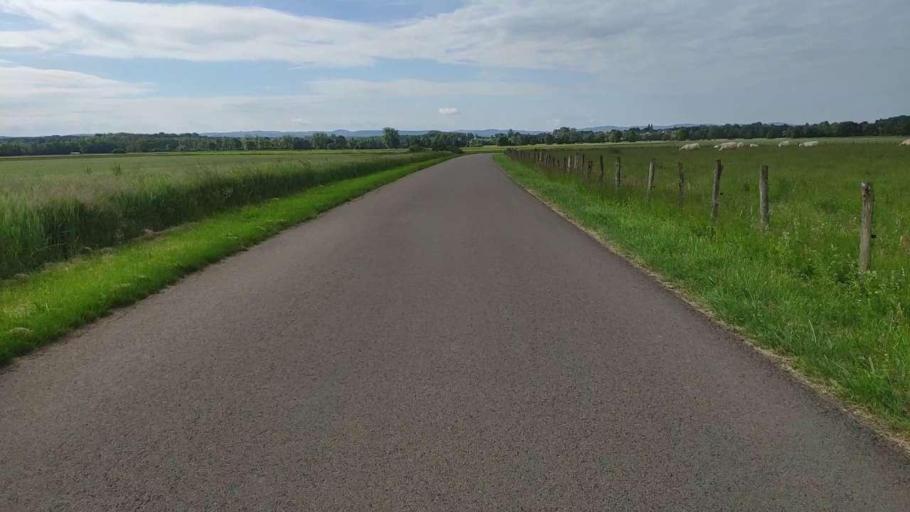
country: FR
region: Franche-Comte
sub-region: Departement du Jura
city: Bletterans
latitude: 46.7306
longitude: 5.4634
